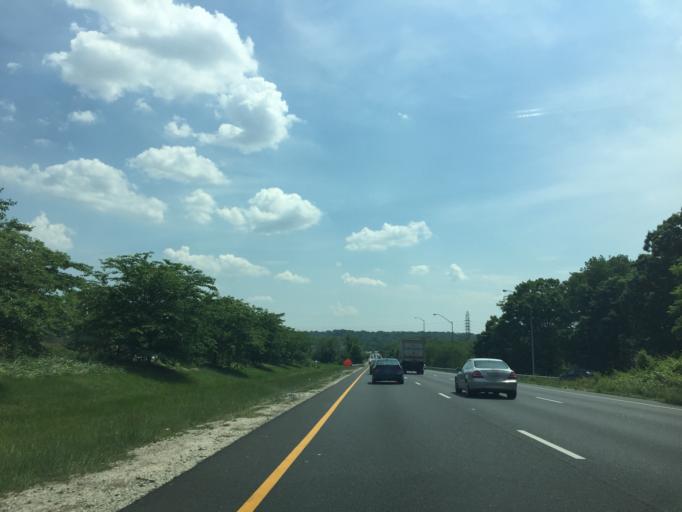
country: US
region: Maryland
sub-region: Baltimore County
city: Baltimore Highlands
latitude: 39.2345
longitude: -76.6497
